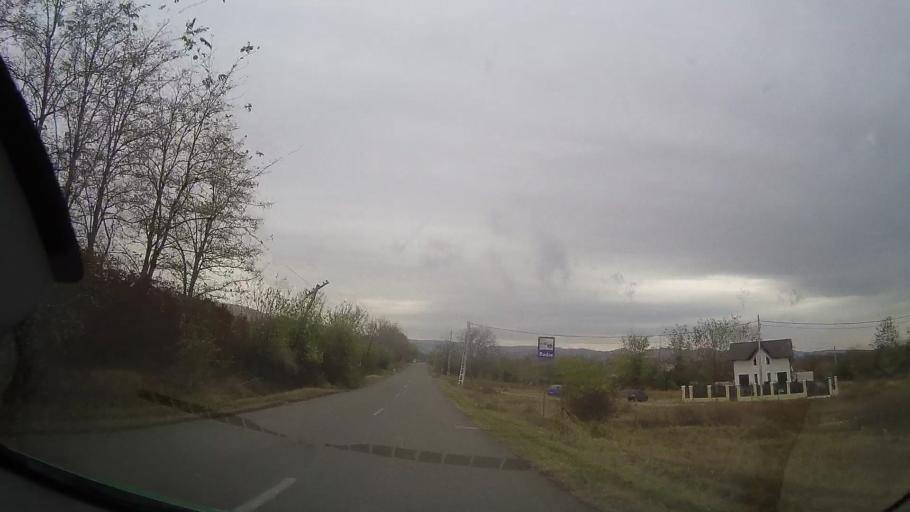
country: RO
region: Prahova
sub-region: Comuna Vadu Sapat
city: Vadu Sapat
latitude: 45.0280
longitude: 26.3838
